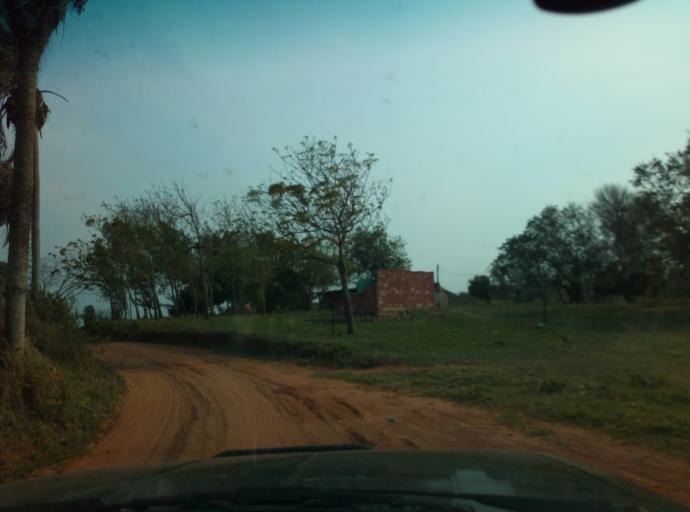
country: PY
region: Caaguazu
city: San Joaquin
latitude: -25.1537
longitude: -56.1047
